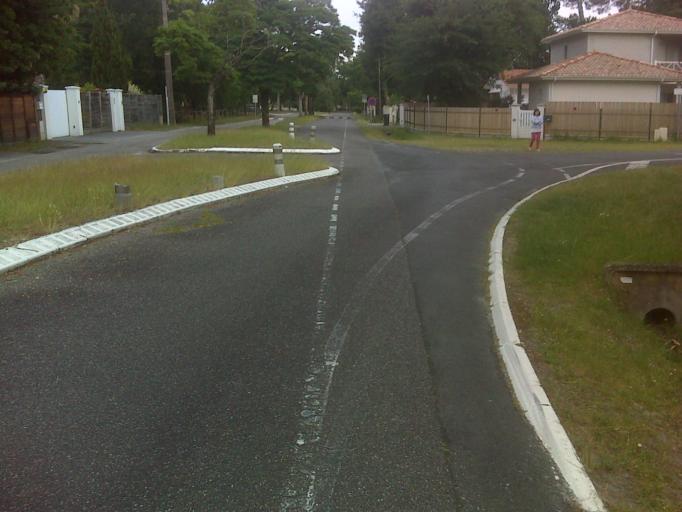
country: FR
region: Aquitaine
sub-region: Departement de la Gironde
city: Ares
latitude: 44.7533
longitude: -1.1276
